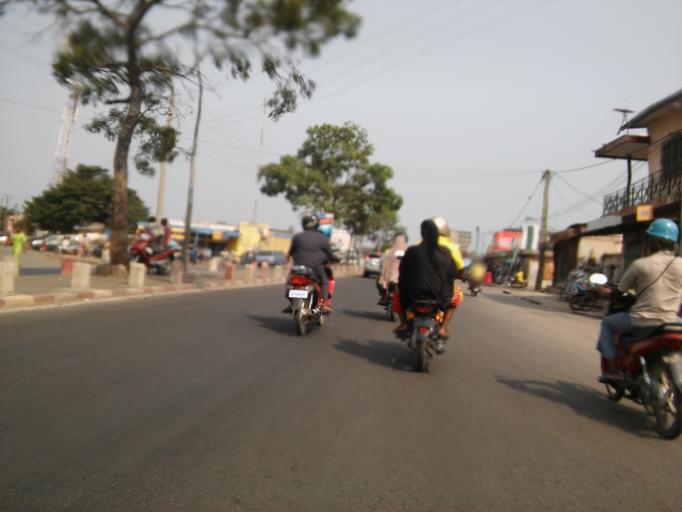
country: BJ
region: Littoral
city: Cotonou
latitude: 6.3701
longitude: 2.4251
